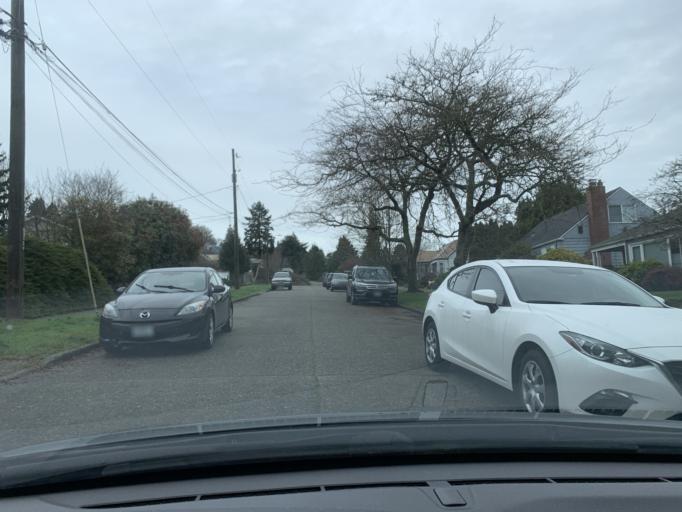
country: US
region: Washington
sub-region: King County
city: White Center
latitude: 47.5587
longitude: -122.3976
